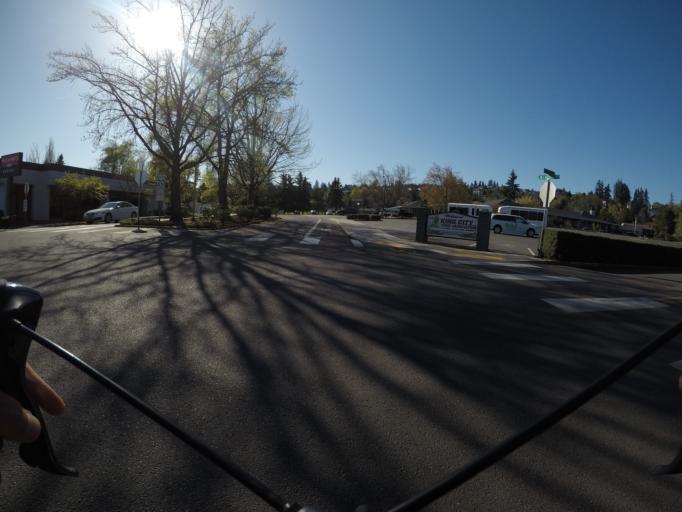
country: US
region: Oregon
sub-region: Washington County
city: King City
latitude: 45.4082
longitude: -122.7957
